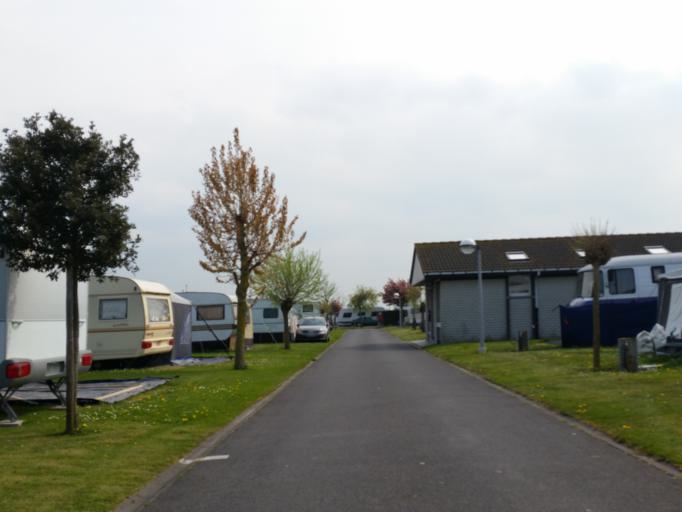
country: BE
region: Flanders
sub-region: Provincie West-Vlaanderen
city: Bredene
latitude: 51.2477
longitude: 2.9676
